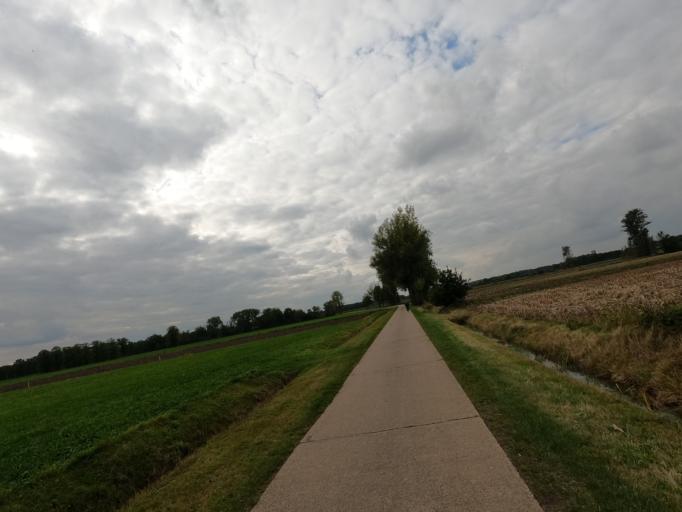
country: BE
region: Flanders
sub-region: Provincie Antwerpen
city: Kasterlee
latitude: 51.2351
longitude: 5.0034
